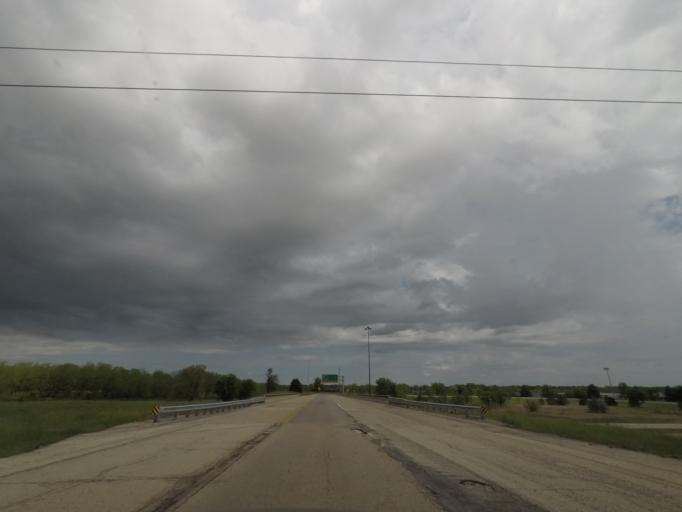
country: US
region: Illinois
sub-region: Winnebago County
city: Cherry Valley
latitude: 42.2194
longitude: -89.0111
